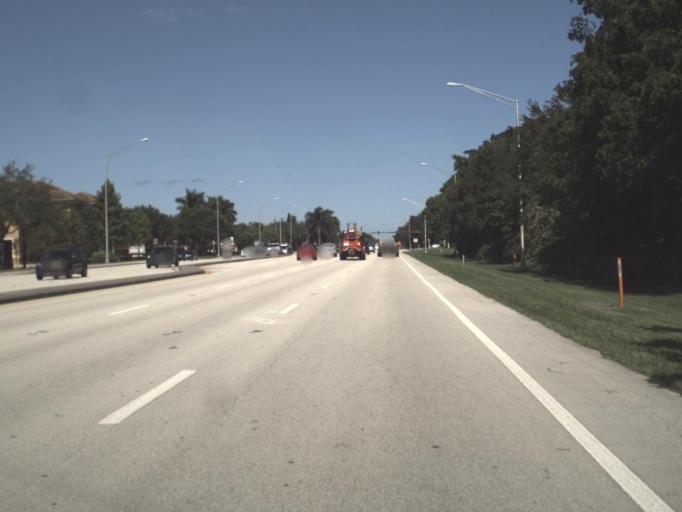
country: US
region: Florida
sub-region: Collier County
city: Naples Park
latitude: 26.2583
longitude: -81.8012
